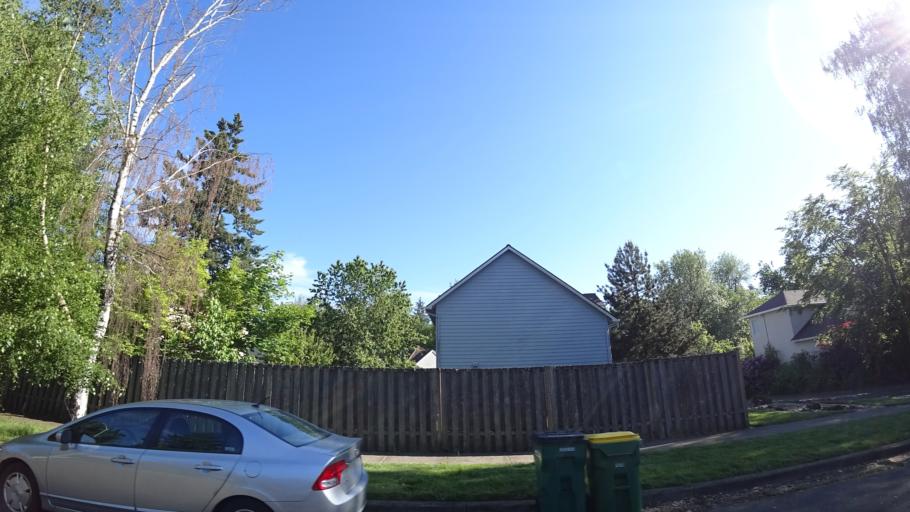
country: US
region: Oregon
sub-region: Washington County
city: Beaverton
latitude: 45.4561
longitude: -122.8120
